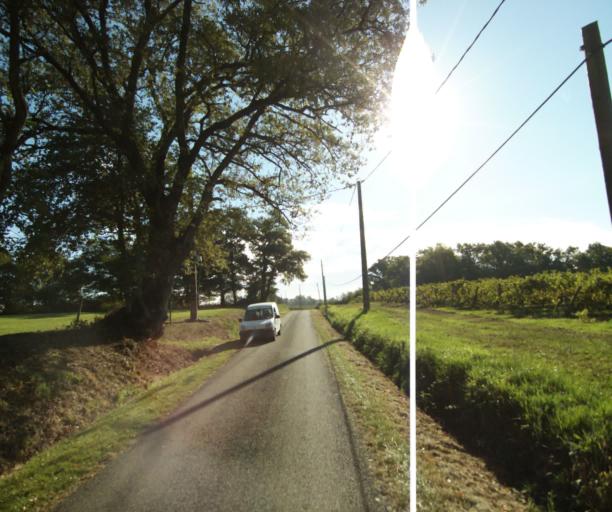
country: FR
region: Midi-Pyrenees
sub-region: Departement du Gers
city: Cazaubon
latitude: 43.9085
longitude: -0.0020
